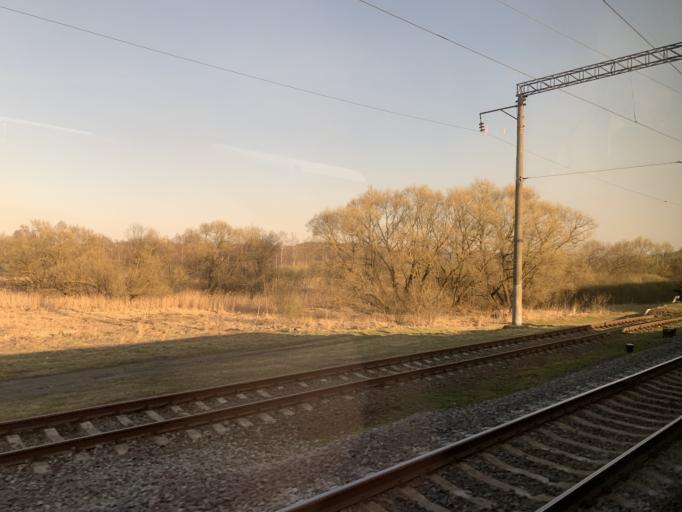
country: BY
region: Minsk
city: Zaslawye
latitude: 54.0038
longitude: 27.2837
